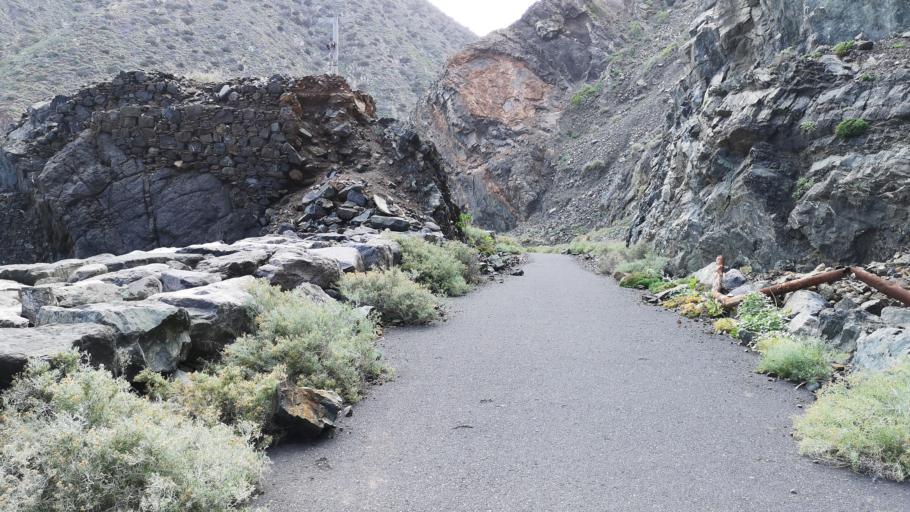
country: ES
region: Canary Islands
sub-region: Provincia de Santa Cruz de Tenerife
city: Vallehermosa
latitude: 28.2053
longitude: -17.2532
